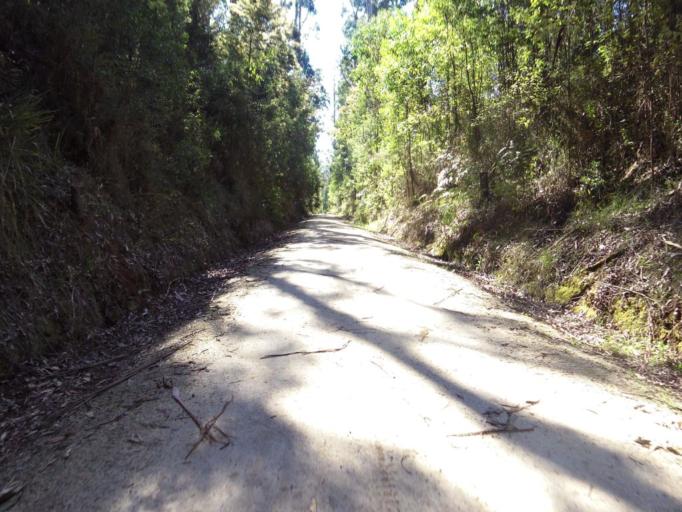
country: AU
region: Victoria
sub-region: Latrobe
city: Moe
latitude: -38.3822
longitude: 146.2431
